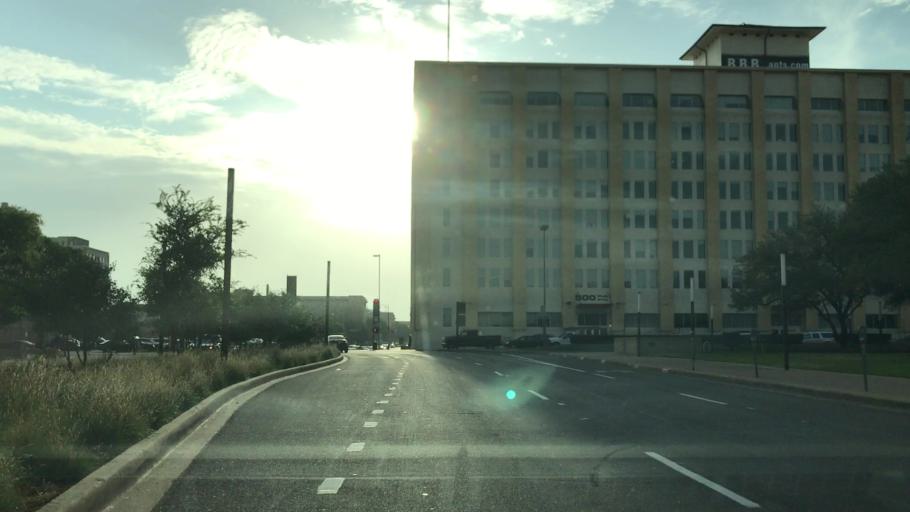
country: US
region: Texas
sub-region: Dallas County
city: Dallas
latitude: 32.7776
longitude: -96.7971
